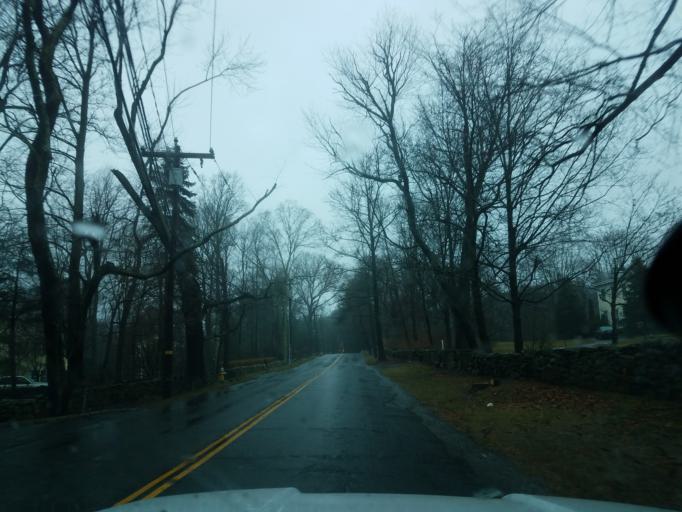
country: US
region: Connecticut
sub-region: Fairfield County
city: Darien
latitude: 41.0862
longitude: -73.4858
